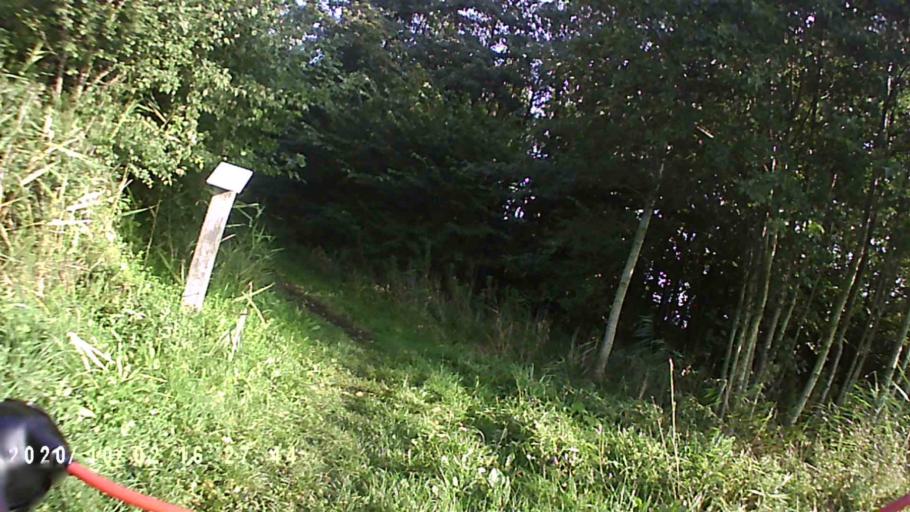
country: NL
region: Groningen
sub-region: Gemeente Zuidhorn
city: Grijpskerk
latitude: 53.2852
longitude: 6.3081
